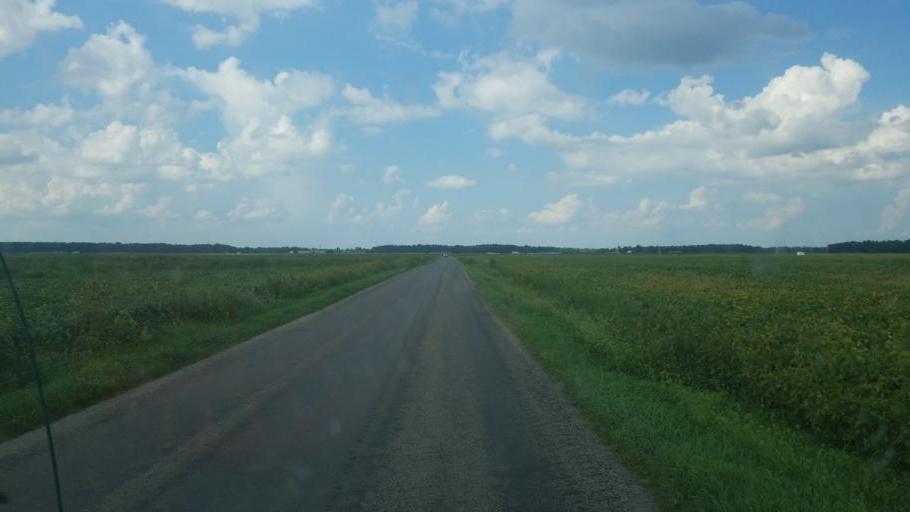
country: US
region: Ohio
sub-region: Huron County
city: Willard
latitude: 41.0136
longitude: -82.7092
